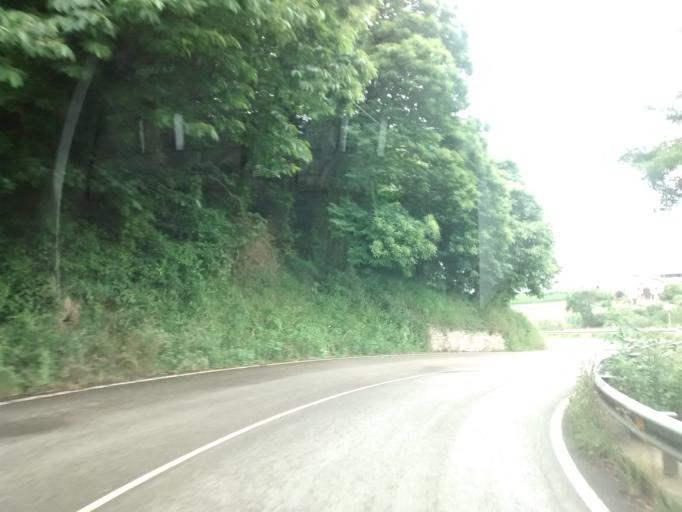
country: ES
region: Cantabria
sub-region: Provincia de Cantabria
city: Santillana
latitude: 43.4107
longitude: -4.0998
